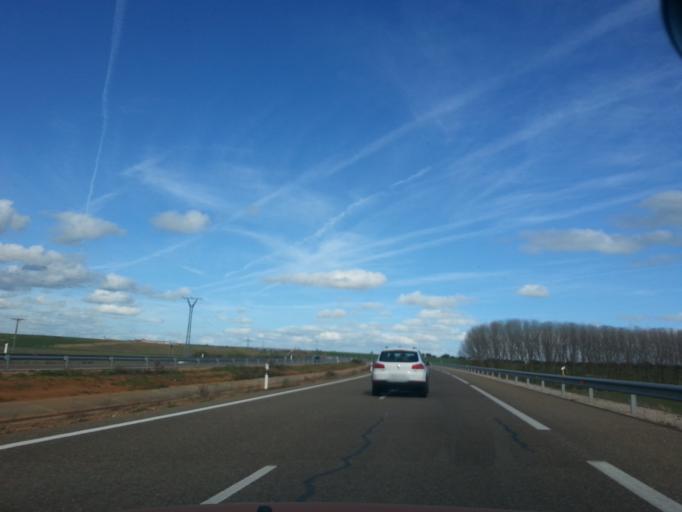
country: ES
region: Castille and Leon
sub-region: Provincia de Salamanca
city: Calzada de Don Diego
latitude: 40.9066
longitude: -5.8772
